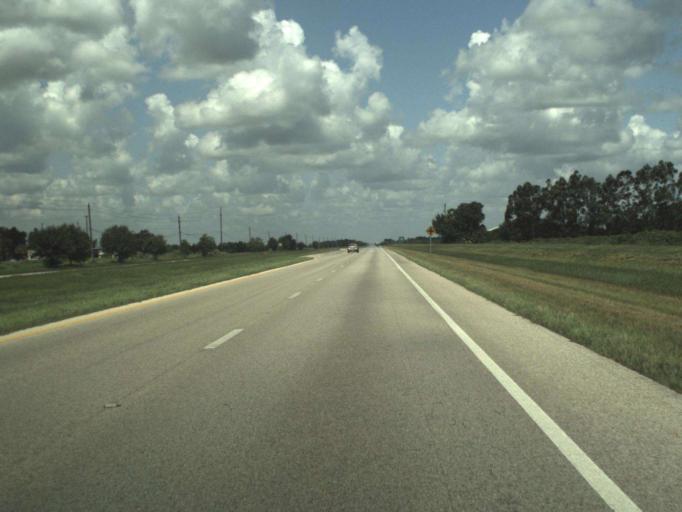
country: US
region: Florida
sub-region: Indian River County
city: Fellsmere
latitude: 27.6404
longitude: -80.6251
